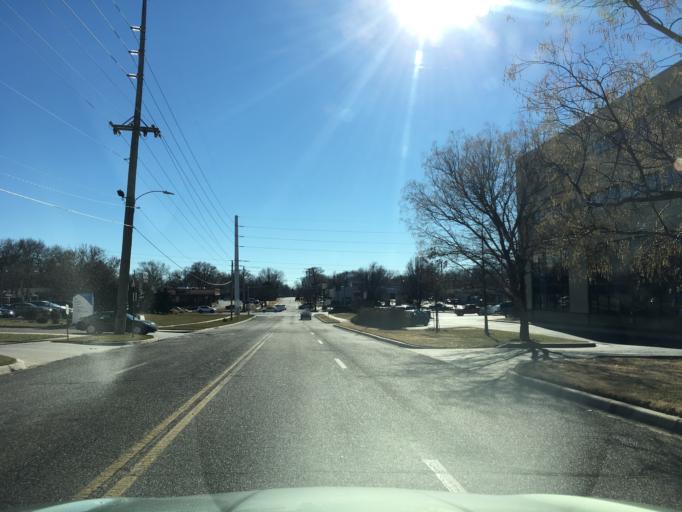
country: US
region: Kansas
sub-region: Sedgwick County
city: Wichita
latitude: 37.6660
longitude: -97.2943
